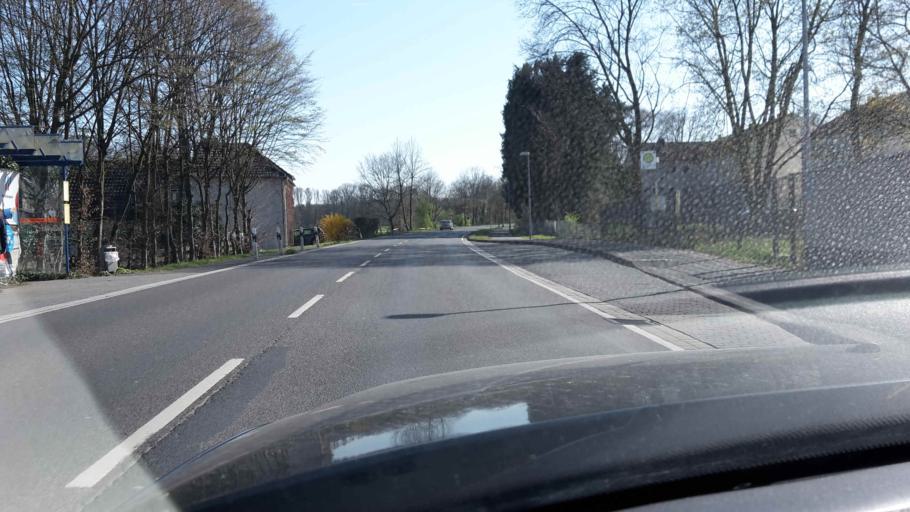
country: DE
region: North Rhine-Westphalia
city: Sankt Augustin
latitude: 50.7627
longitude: 7.2154
